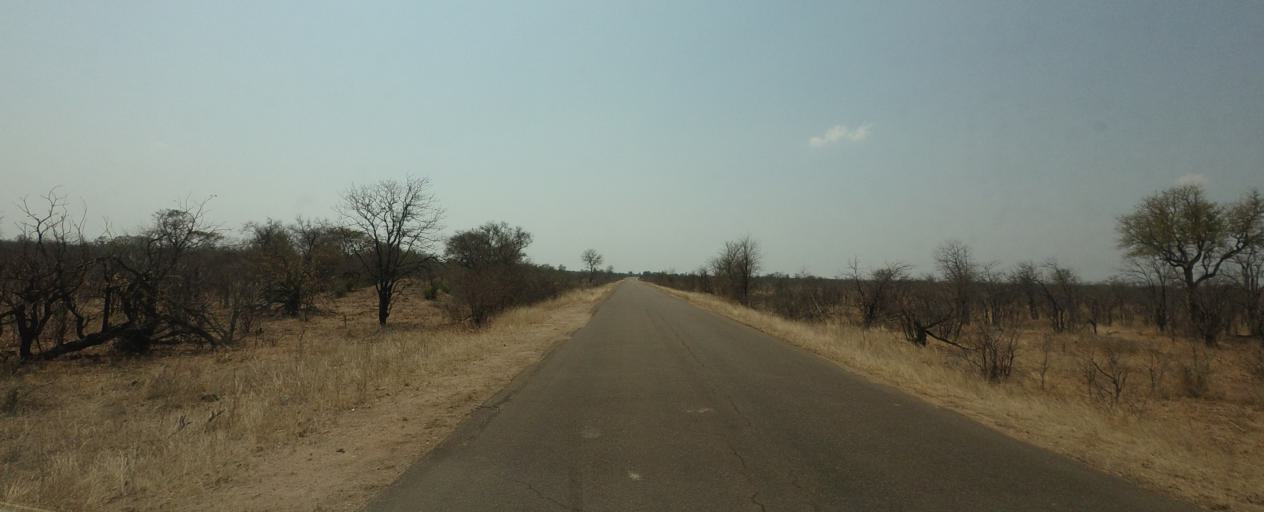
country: ZA
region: Limpopo
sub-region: Mopani District Municipality
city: Phalaborwa
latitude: -23.3815
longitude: 31.3256
